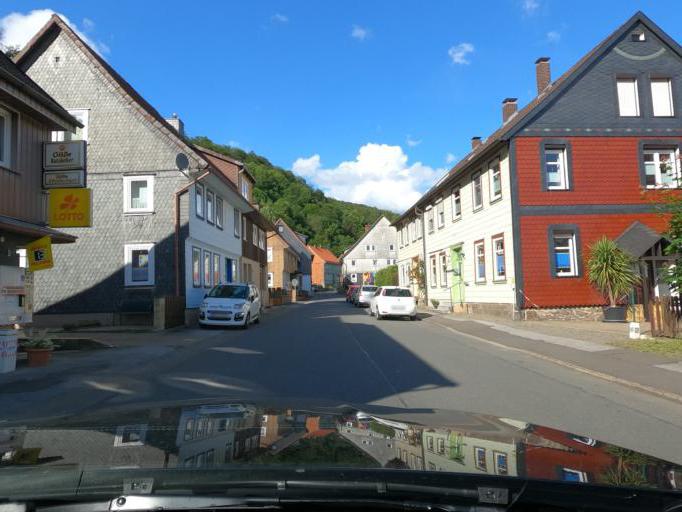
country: DE
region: Lower Saxony
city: Osterode am Harz
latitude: 51.7547
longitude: 10.2928
